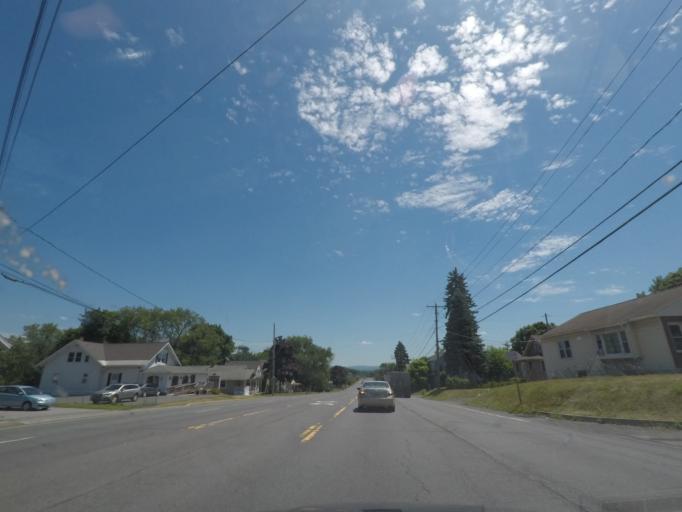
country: US
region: New York
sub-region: Albany County
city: Watervliet
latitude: 42.7465
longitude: -73.7579
